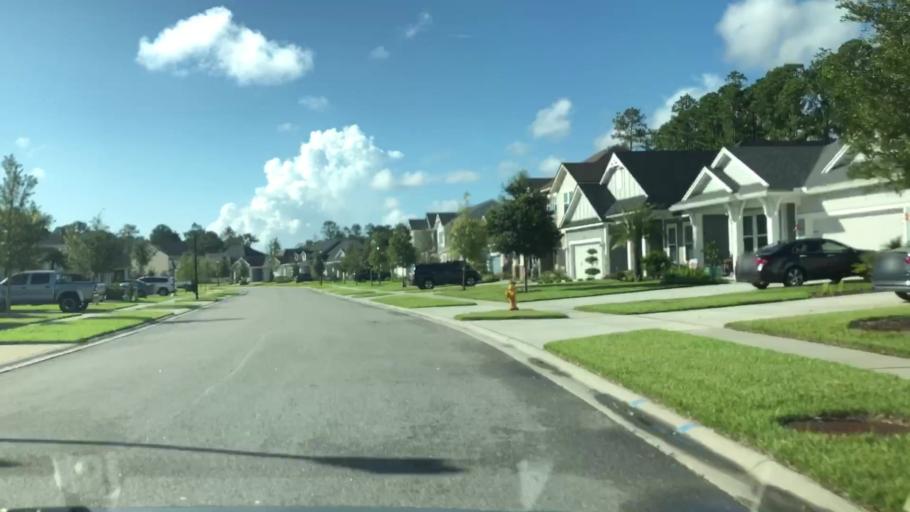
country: US
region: Florida
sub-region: Saint Johns County
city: Palm Valley
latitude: 30.1268
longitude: -81.4103
